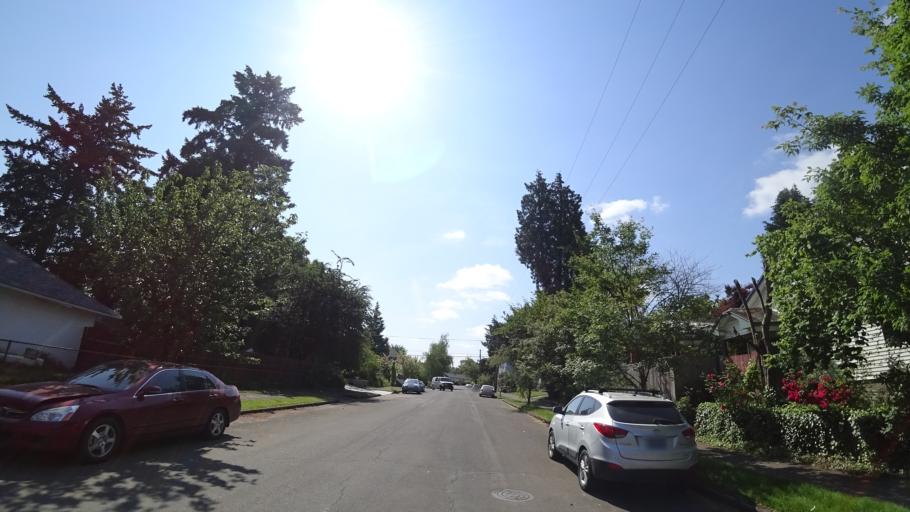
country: US
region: Oregon
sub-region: Multnomah County
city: Portland
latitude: 45.5710
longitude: -122.6534
